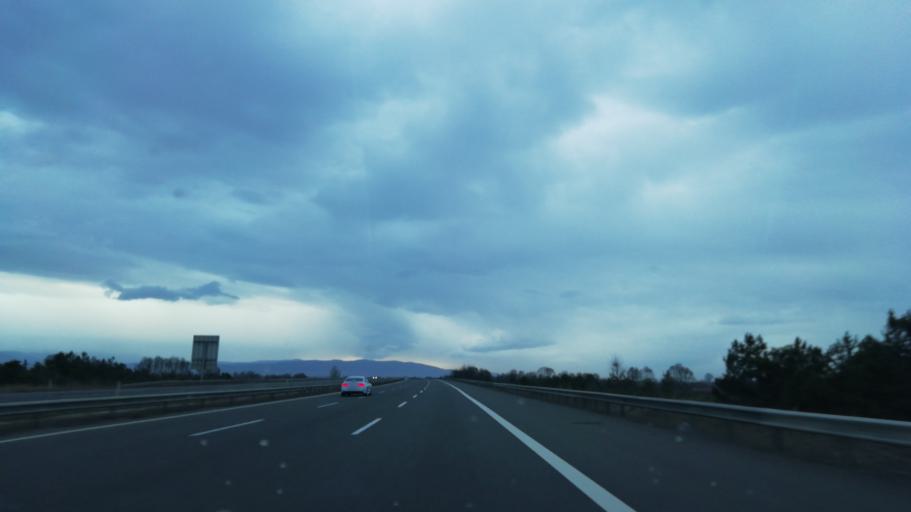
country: TR
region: Bolu
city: Gerede
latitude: 40.7404
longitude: 32.1656
